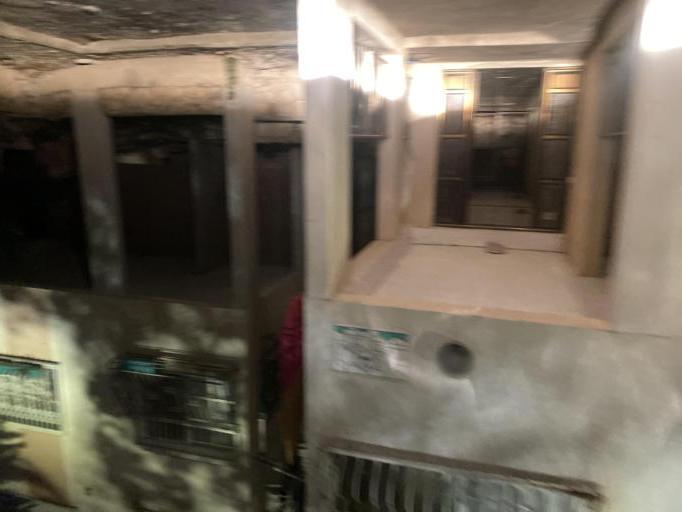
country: IL
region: Haifa
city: Daliyat el Karmil
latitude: 32.6558
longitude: 35.1032
